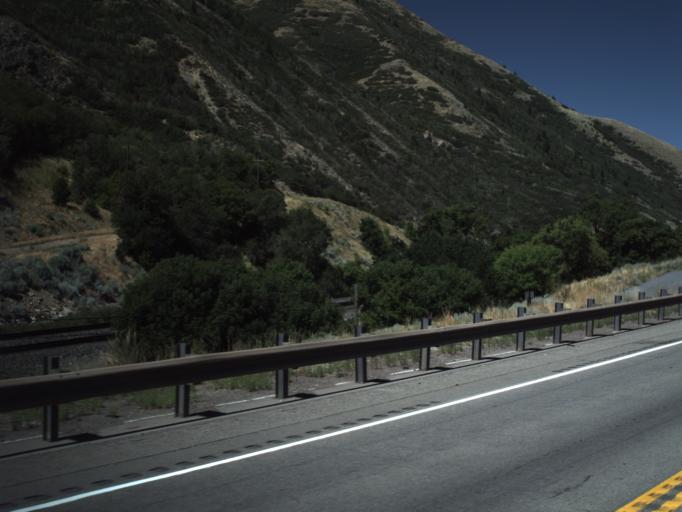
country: US
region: Utah
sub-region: Utah County
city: Mapleton
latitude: 40.0577
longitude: -111.5624
